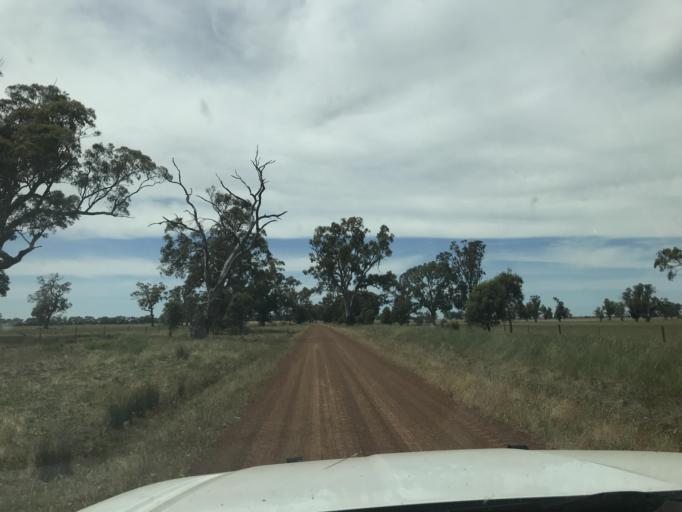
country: AU
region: South Australia
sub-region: Wattle Range
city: Penola
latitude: -37.0067
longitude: 141.4678
